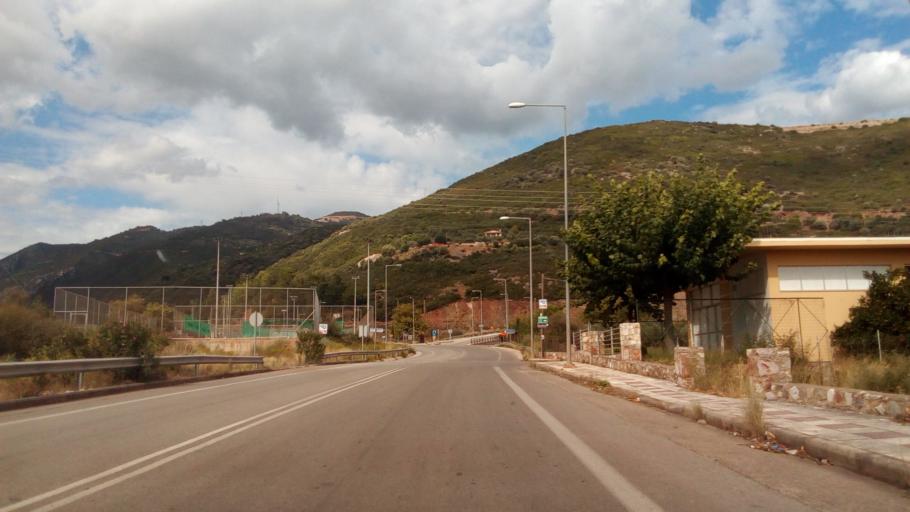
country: GR
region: West Greece
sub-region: Nomos Aitolias kai Akarnanias
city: Nafpaktos
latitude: 38.4110
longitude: 21.8424
